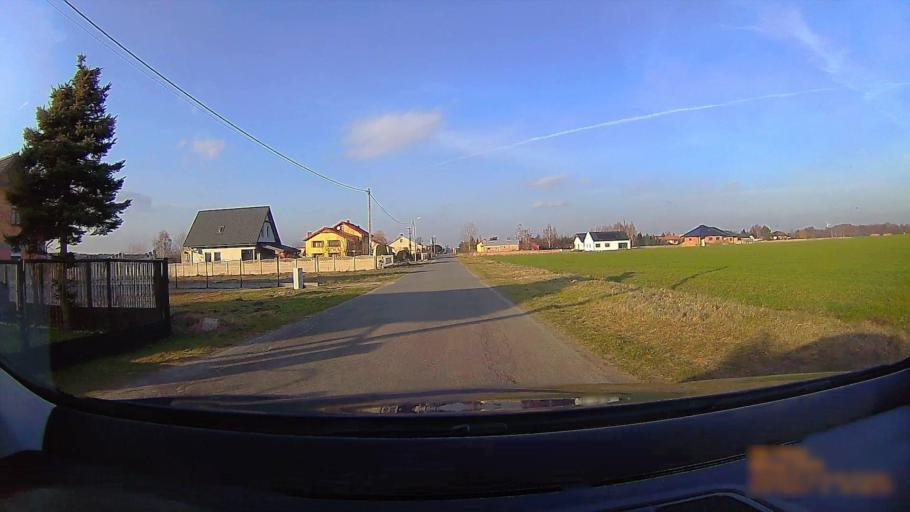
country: PL
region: Greater Poland Voivodeship
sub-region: Konin
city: Konin
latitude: 52.1796
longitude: 18.3008
